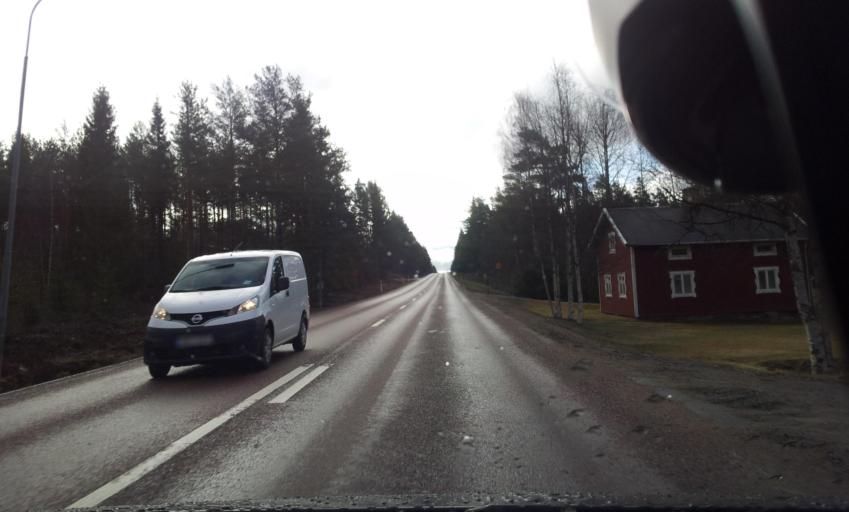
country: SE
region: Gaevleborg
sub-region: Ljusdals Kommun
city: Ljusdal
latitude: 61.8244
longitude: 16.1442
